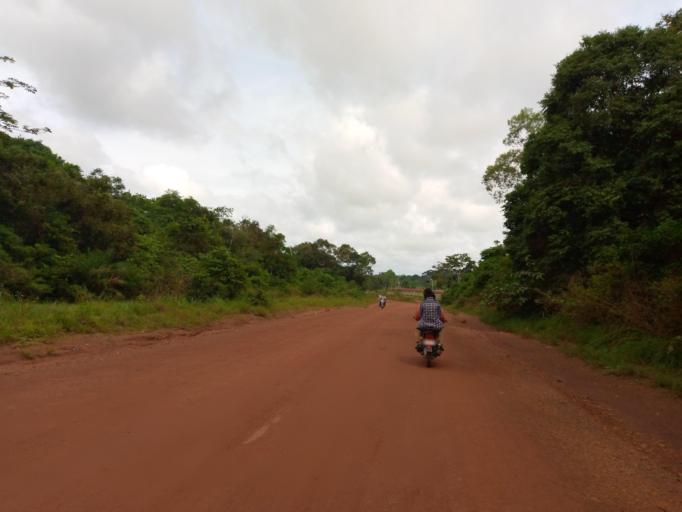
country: SL
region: Southern Province
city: Mogbwemo
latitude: 7.7656
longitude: -12.2998
